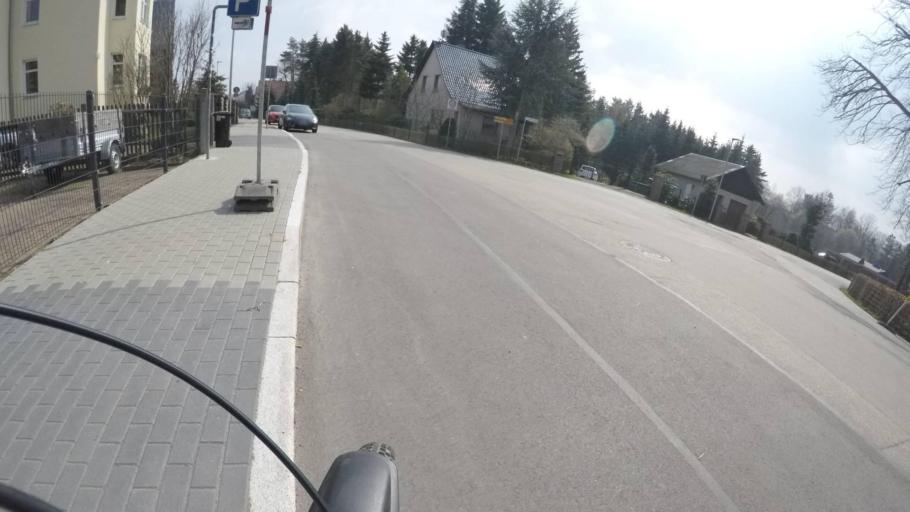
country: DE
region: Saxony
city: Limbach-Oberfrohna
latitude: 50.8545
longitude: 12.7551
